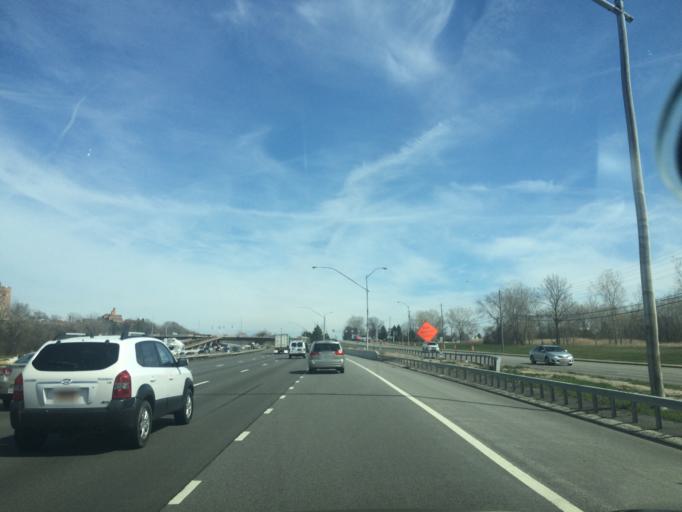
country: US
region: New York
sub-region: Monroe County
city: Rochester
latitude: 43.1136
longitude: -77.6285
